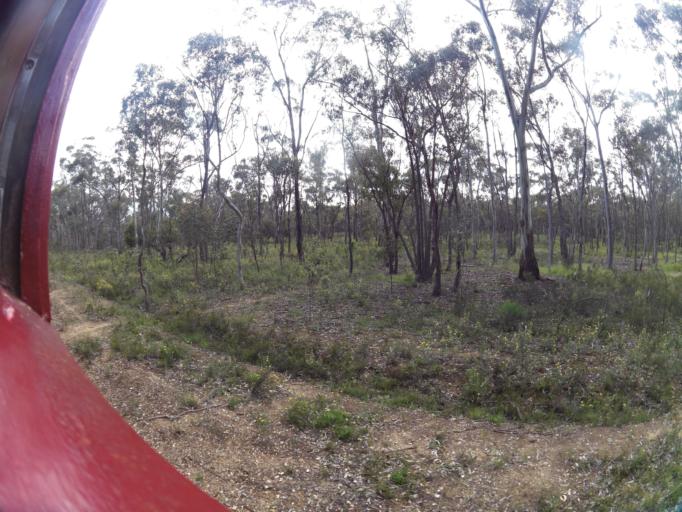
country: AU
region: Victoria
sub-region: Mount Alexander
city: Castlemaine
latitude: -37.0522
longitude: 144.1864
